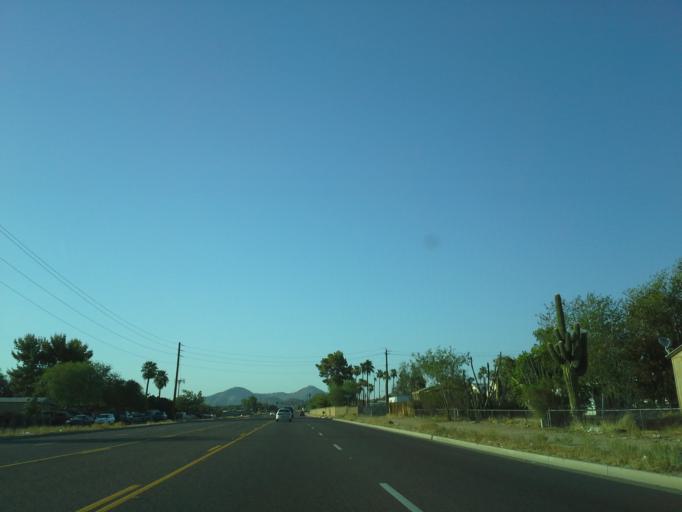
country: US
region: Arizona
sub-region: Pinal County
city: Apache Junction
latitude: 33.4103
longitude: -111.6326
